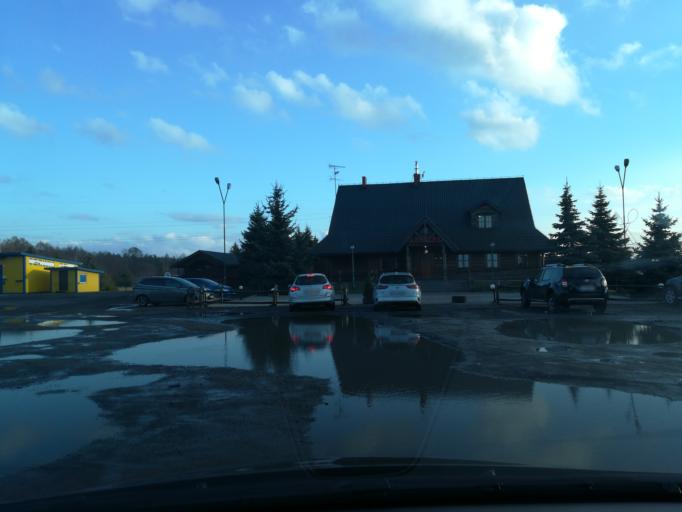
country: PL
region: Lodz Voivodeship
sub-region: Powiat piotrkowski
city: Wola Krzysztoporska
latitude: 51.3441
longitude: 19.6012
